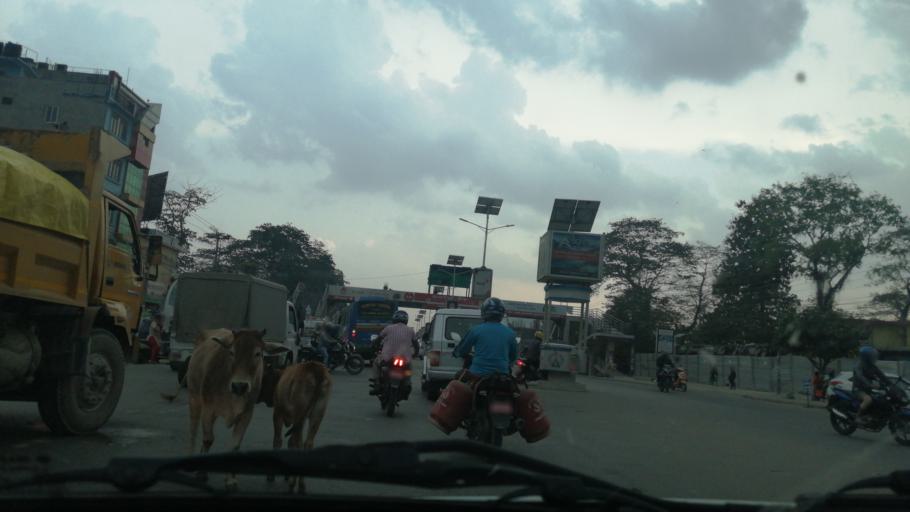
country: NP
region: Western Region
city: Butwal
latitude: 27.6966
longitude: 83.4651
